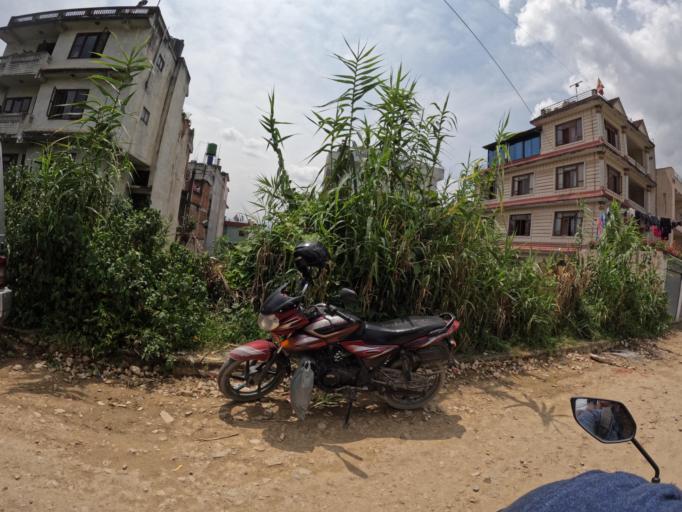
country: NP
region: Central Region
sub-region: Bagmati Zone
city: Kathmandu
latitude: 27.6810
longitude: 85.3731
